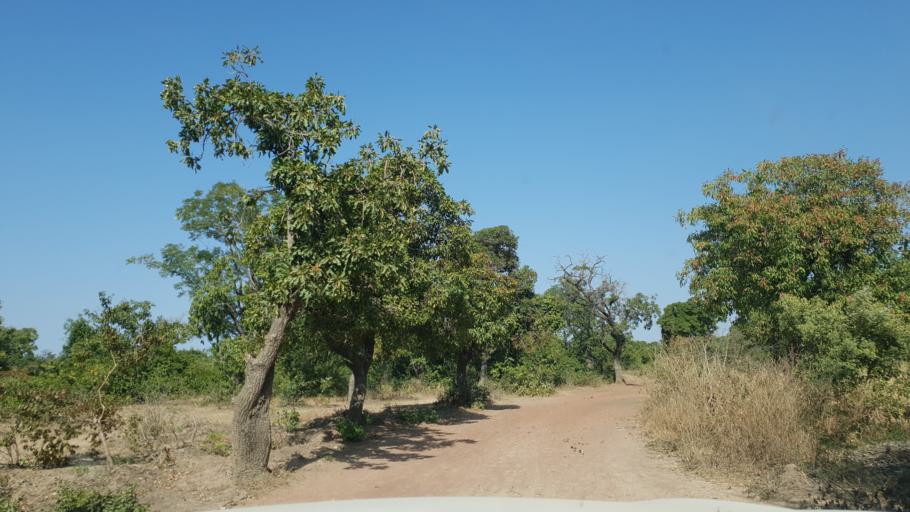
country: ML
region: Sikasso
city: Yorosso
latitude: 12.2713
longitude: -4.6949
